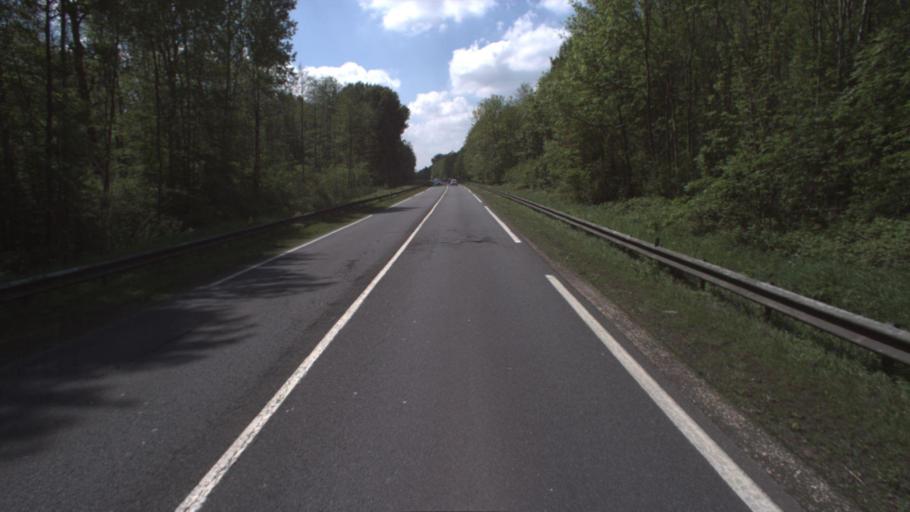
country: FR
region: Ile-de-France
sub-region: Departement de Seine-et-Marne
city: Chaumes-en-Brie
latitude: 48.6887
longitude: 2.8174
